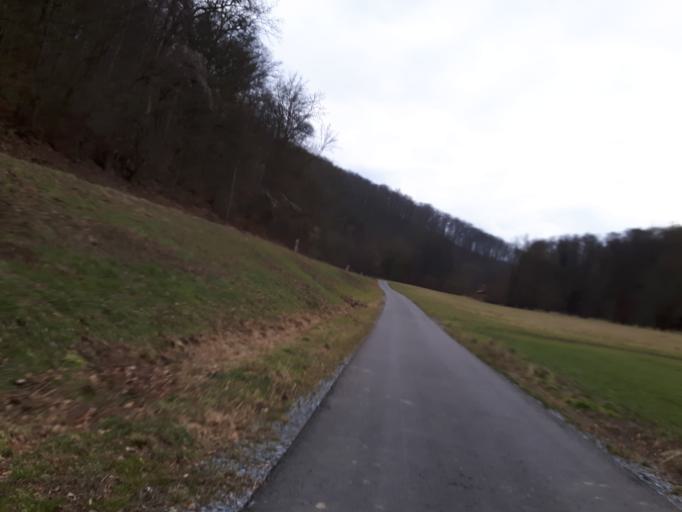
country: DE
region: Baden-Wuerttemberg
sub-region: Regierungsbezirk Stuttgart
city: Zweiflingen
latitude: 49.2419
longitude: 9.4614
